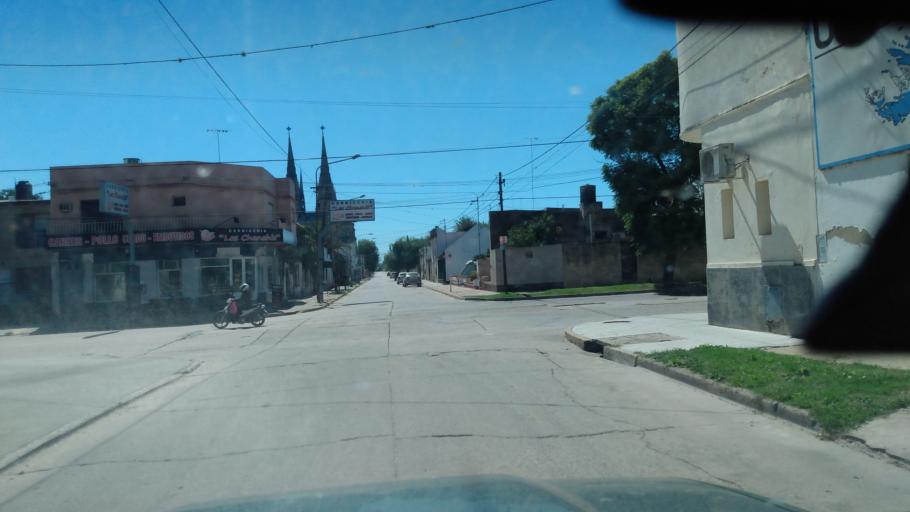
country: AR
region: Buenos Aires
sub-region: Partido de Lujan
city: Lujan
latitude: -34.5687
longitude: -59.1227
